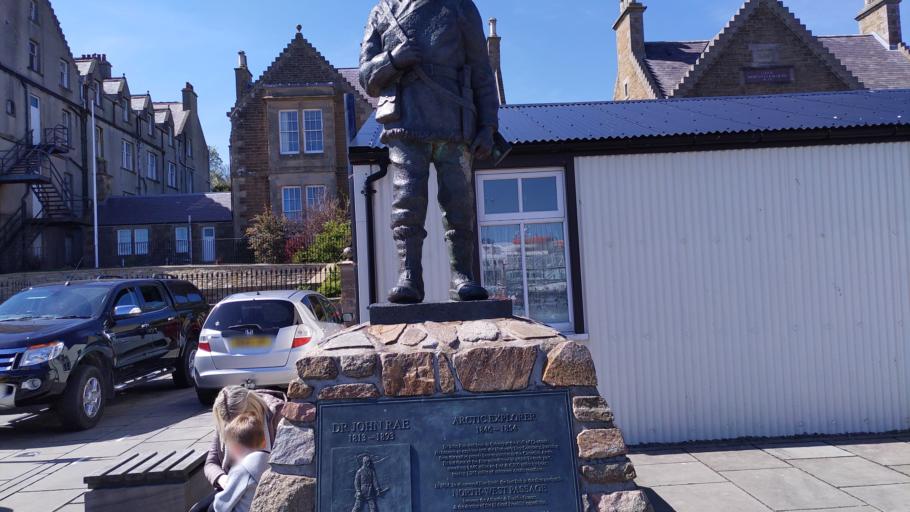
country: GB
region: Scotland
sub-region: Orkney Islands
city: Stromness
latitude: 58.9634
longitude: -3.2975
